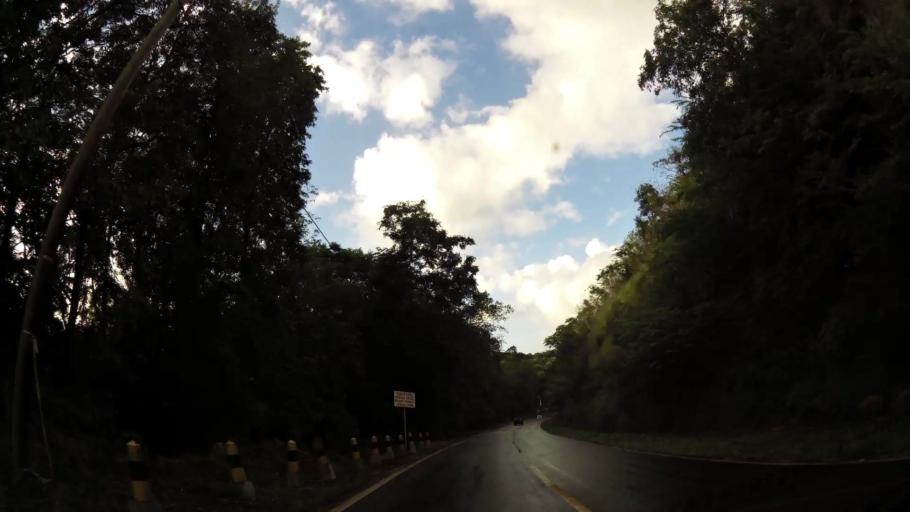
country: DM
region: Saint Peter
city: Colihaut
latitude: 15.5319
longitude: -61.4743
